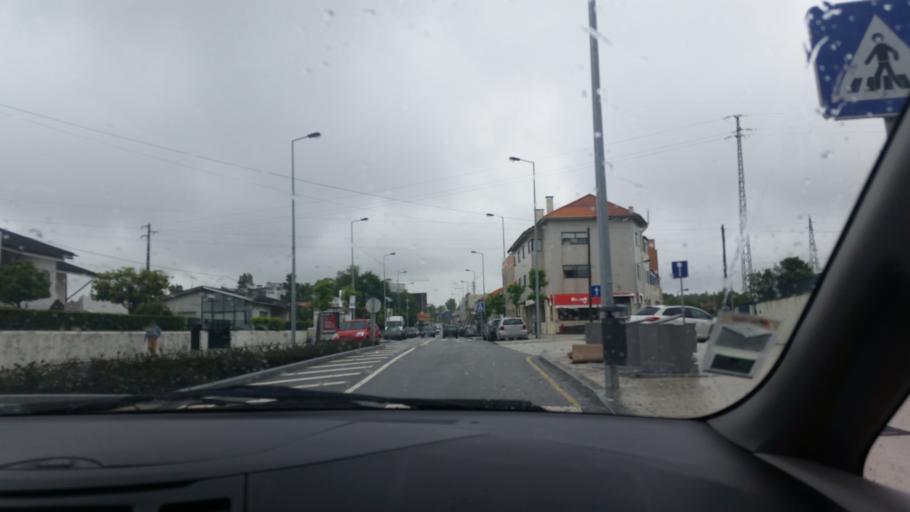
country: PT
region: Porto
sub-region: Matosinhos
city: Matosinhos
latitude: 41.1864
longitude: -8.6775
